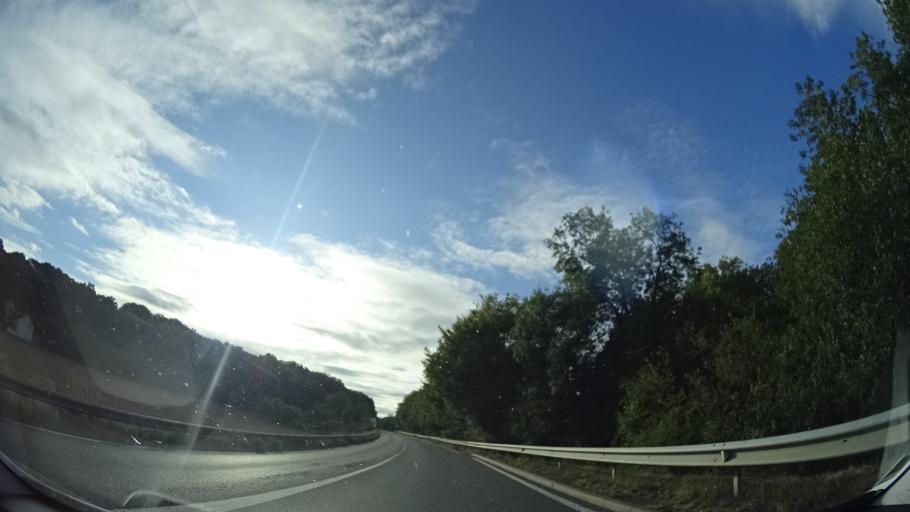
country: FR
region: Centre
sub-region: Departement du Loir-et-Cher
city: Moree
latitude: 47.8933
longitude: 1.1773
